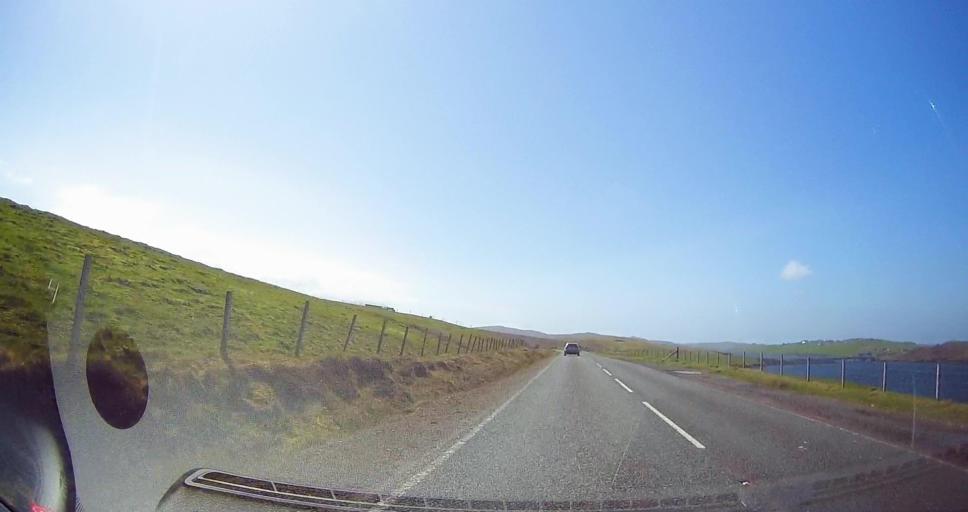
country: GB
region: Scotland
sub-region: Shetland Islands
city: Sandwick
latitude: 60.1130
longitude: -1.2946
